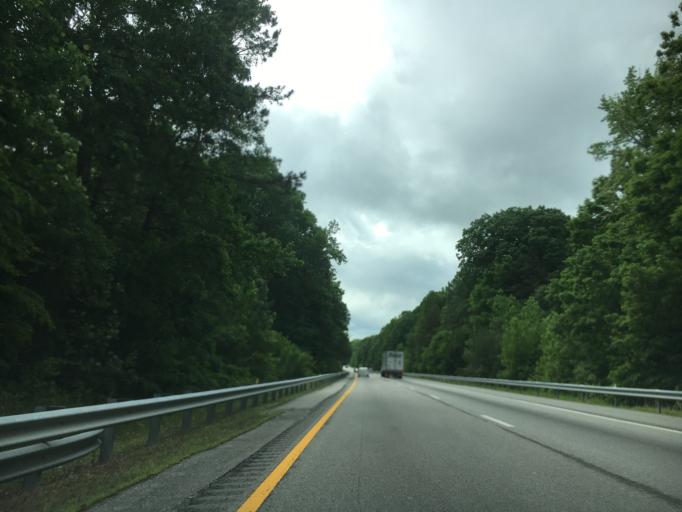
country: US
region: Virginia
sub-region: Mecklenburg County
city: South Hill
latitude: 36.7688
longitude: -78.0602
